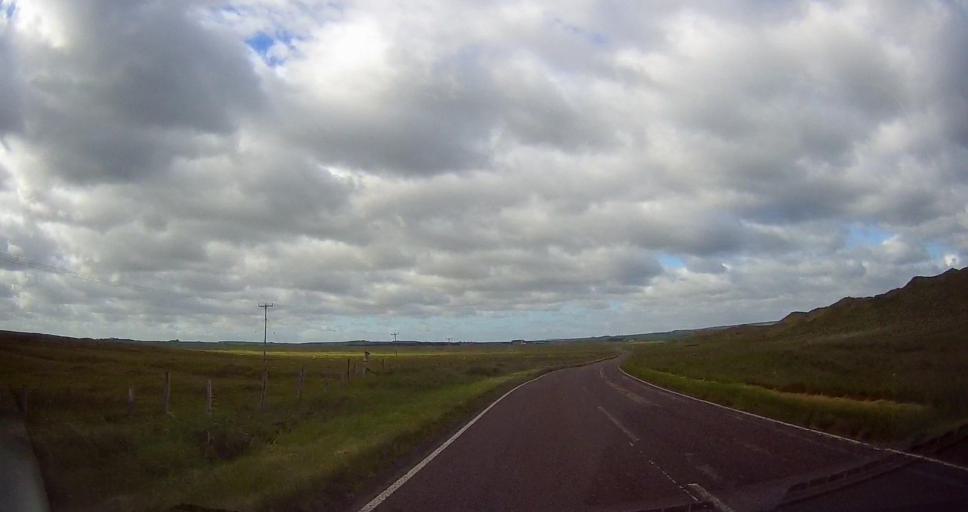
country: GB
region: Scotland
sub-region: Highland
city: Thurso
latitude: 58.6080
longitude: -3.3441
